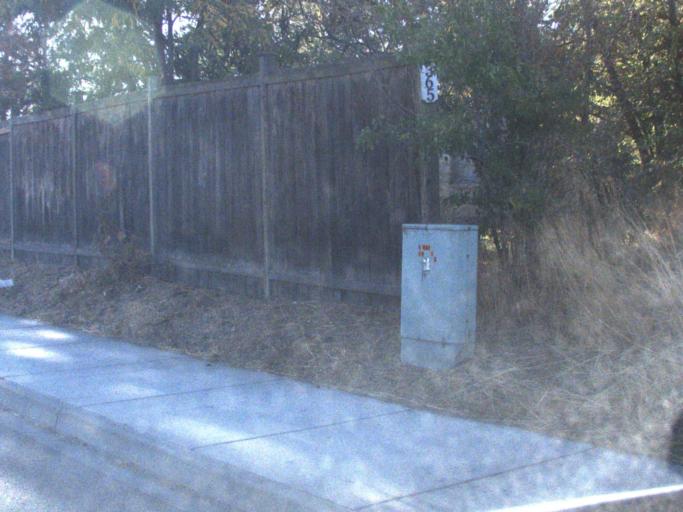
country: US
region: Washington
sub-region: Benton County
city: West Richland
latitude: 46.2994
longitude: -119.3443
